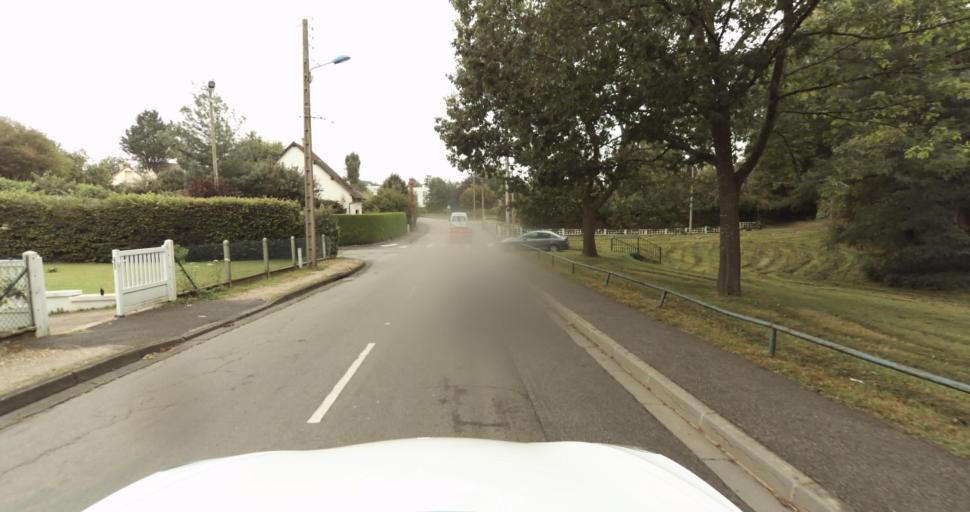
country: FR
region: Haute-Normandie
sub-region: Departement de l'Eure
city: Evreux
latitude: 49.0329
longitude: 1.1393
